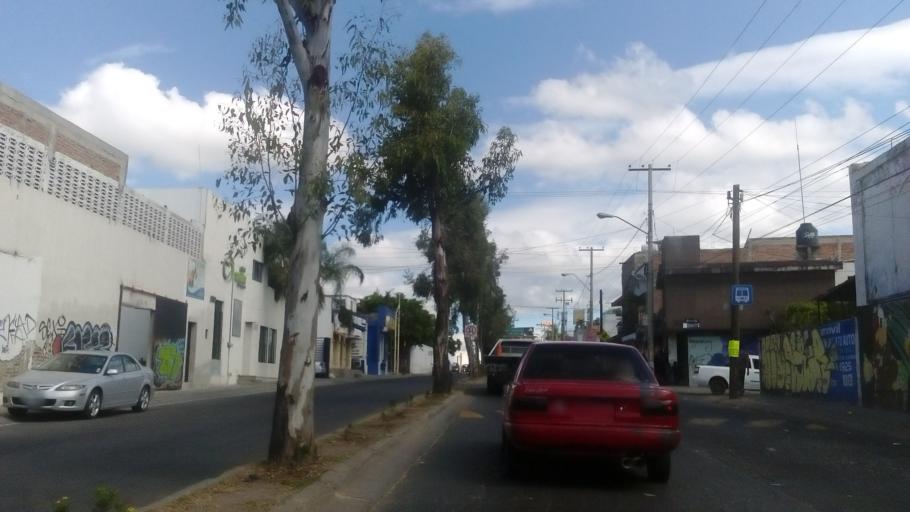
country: MX
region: Guanajuato
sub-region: Leon
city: La Ermita
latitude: 21.1440
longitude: -101.7019
